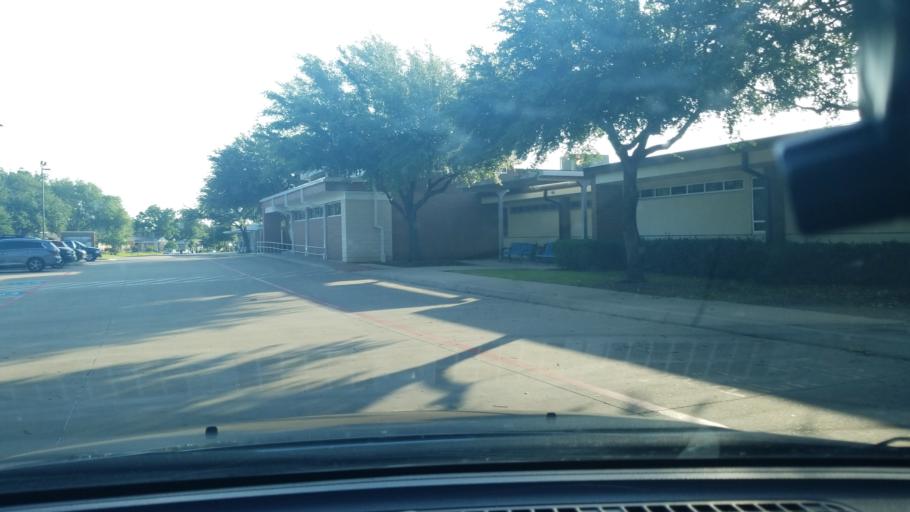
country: US
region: Texas
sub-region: Dallas County
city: Mesquite
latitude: 32.7989
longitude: -96.6381
